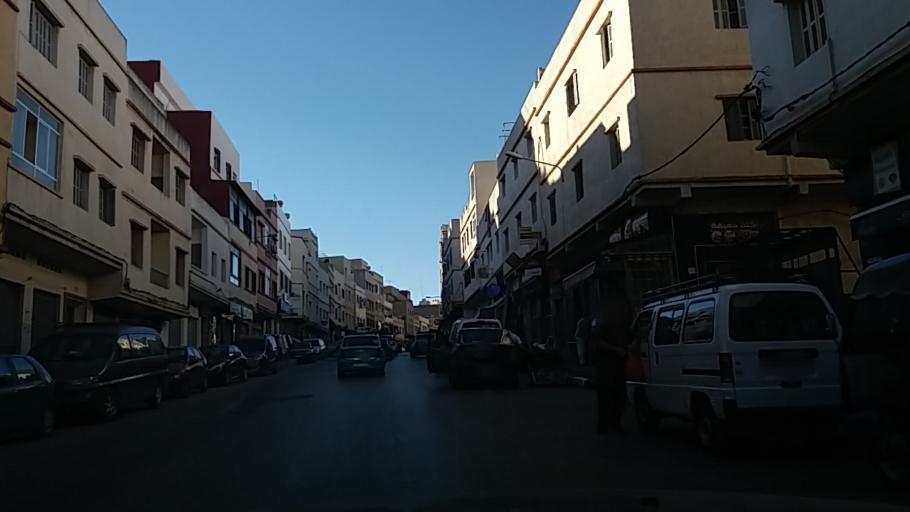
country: MA
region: Tanger-Tetouan
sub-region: Tanger-Assilah
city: Tangier
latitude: 35.7719
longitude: -5.8217
